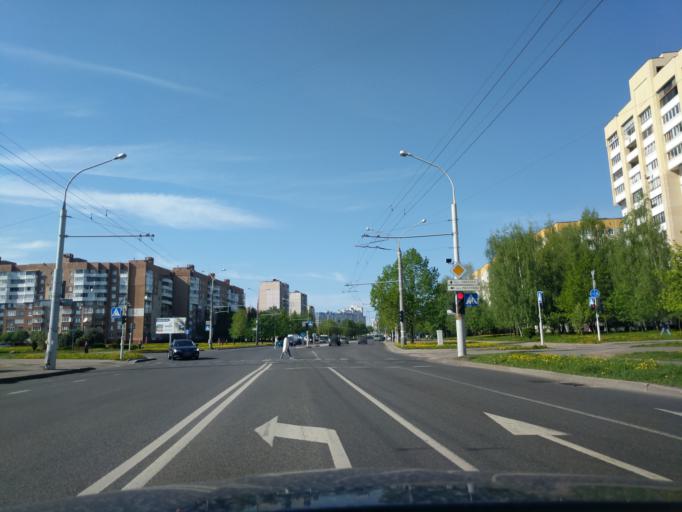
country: BY
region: Minsk
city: Novoye Medvezhino
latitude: 53.8951
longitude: 27.4351
